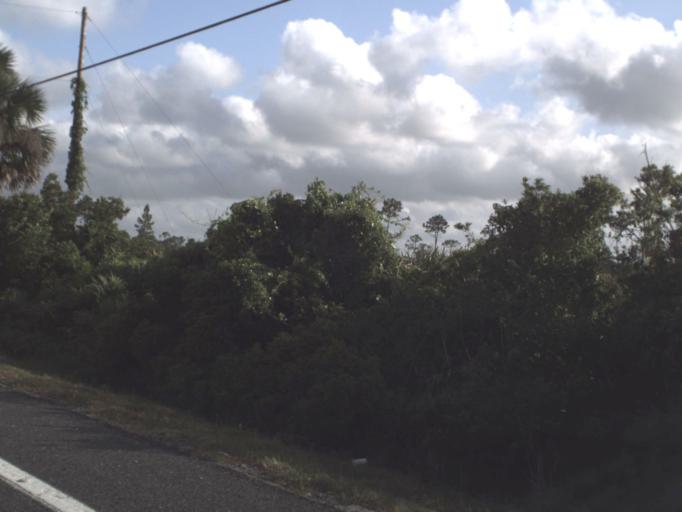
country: US
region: Florida
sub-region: Brevard County
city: Mims
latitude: 28.7524
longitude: -80.8734
